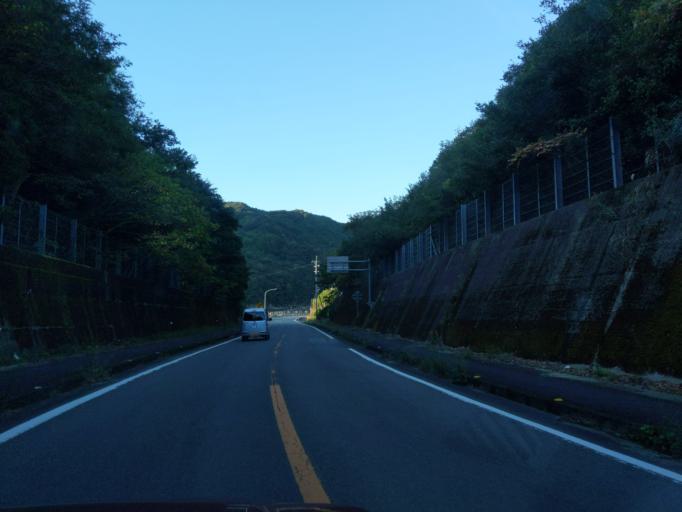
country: JP
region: Kochi
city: Muroto-misakicho
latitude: 33.5875
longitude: 134.3513
